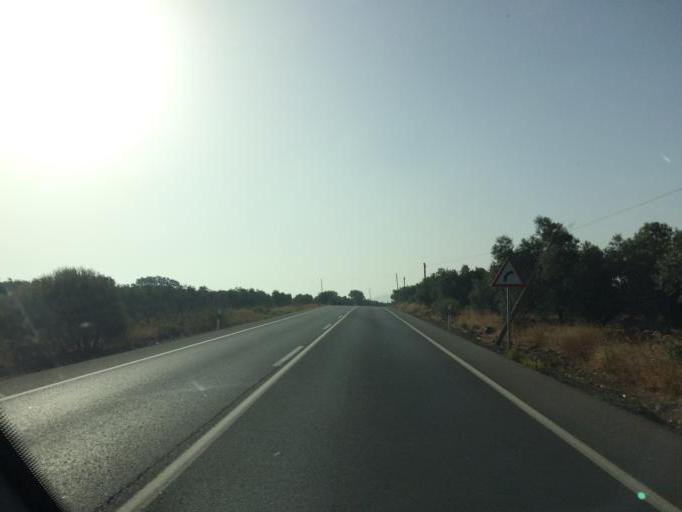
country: ES
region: Andalusia
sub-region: Provincia de Malaga
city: Humilladero
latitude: 37.0573
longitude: -4.6781
